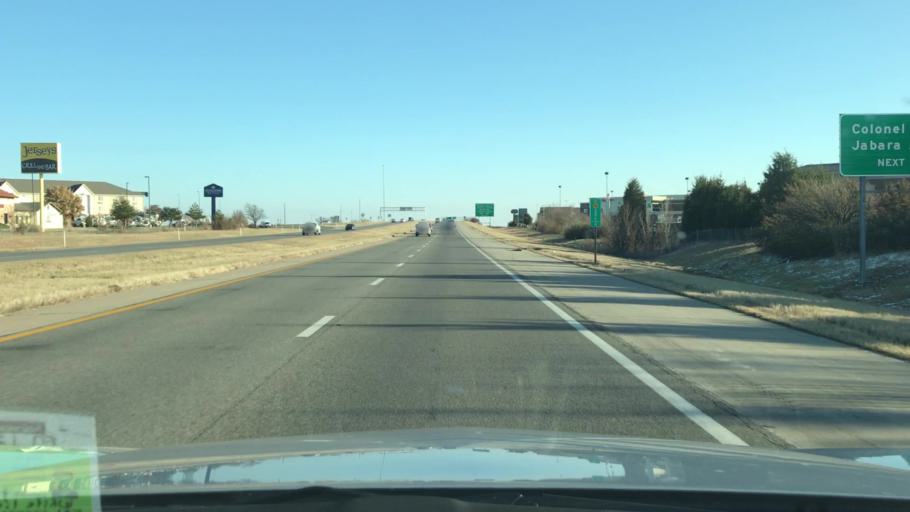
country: US
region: Kansas
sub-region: Sedgwick County
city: Bellaire
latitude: 37.7417
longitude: -97.2314
